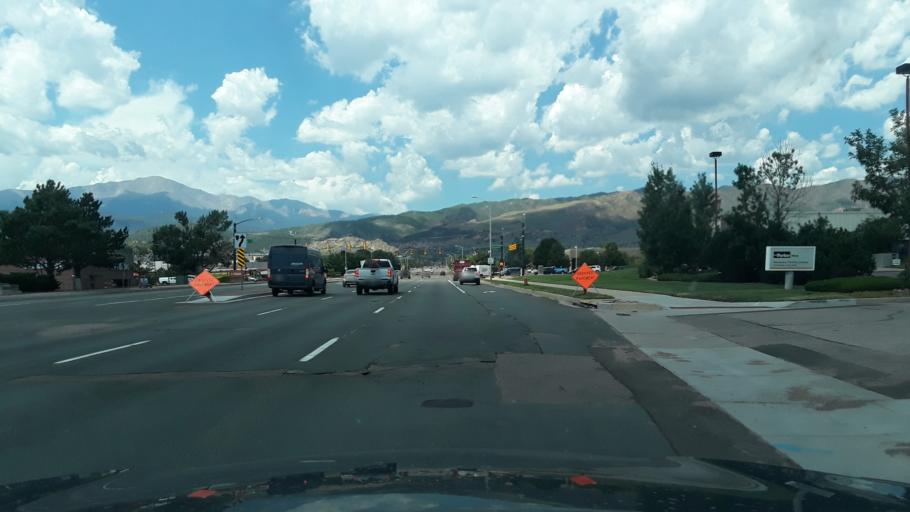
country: US
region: Colorado
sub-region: El Paso County
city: Colorado Springs
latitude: 38.8967
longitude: -104.8483
